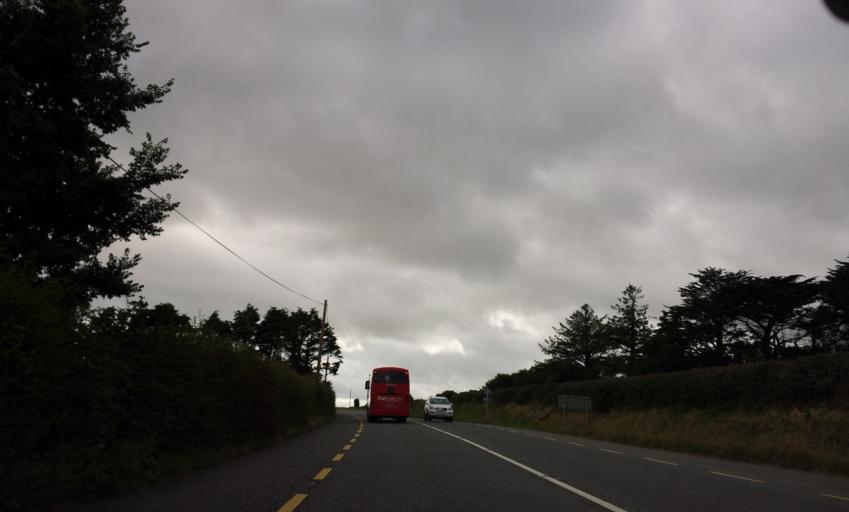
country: IE
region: Munster
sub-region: County Cork
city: Youghal
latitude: 51.9860
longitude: -7.7492
